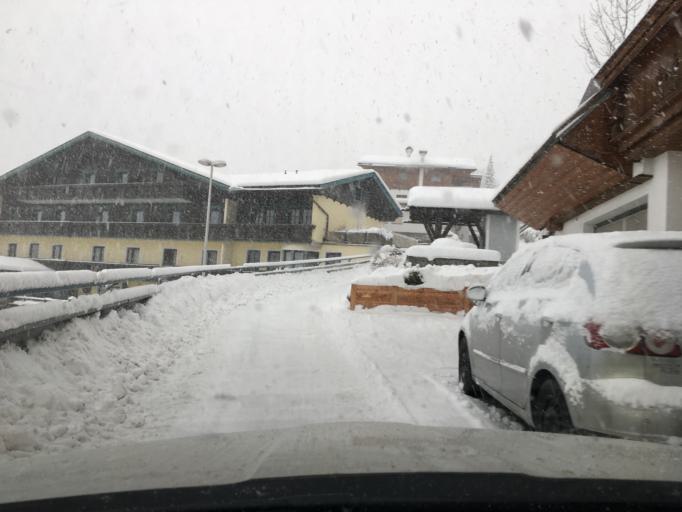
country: AT
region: Tyrol
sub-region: Politischer Bezirk Schwaz
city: Mayrhofen
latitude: 47.1522
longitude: 11.8186
